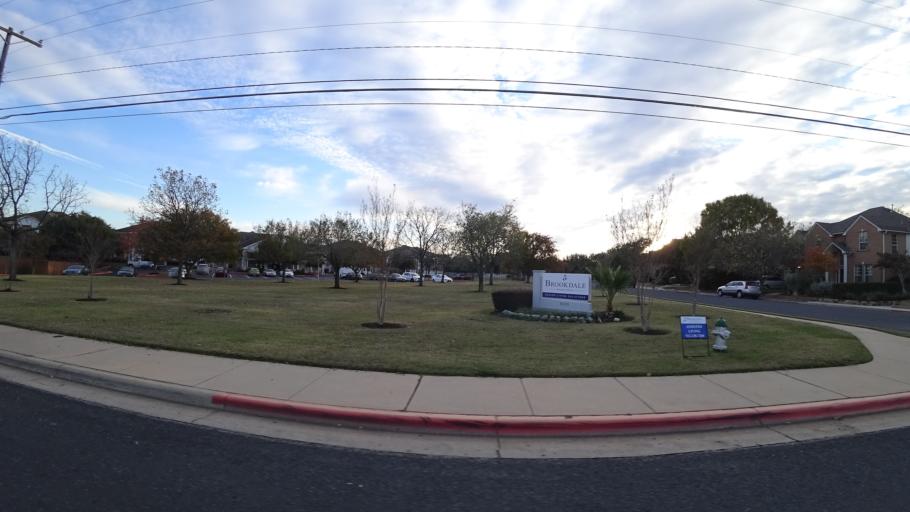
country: US
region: Texas
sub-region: Williamson County
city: Brushy Creek
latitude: 30.4918
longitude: -97.7352
